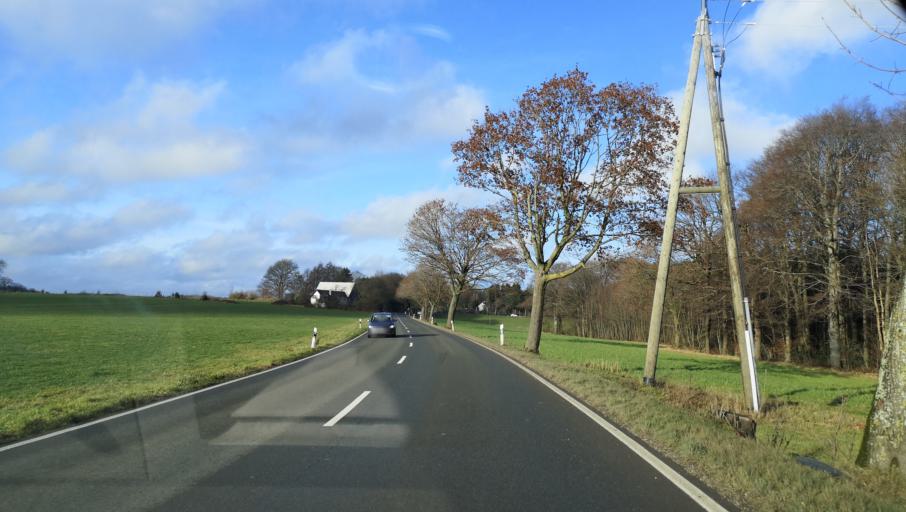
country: DE
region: North Rhine-Westphalia
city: Radevormwald
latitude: 51.2315
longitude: 7.3685
